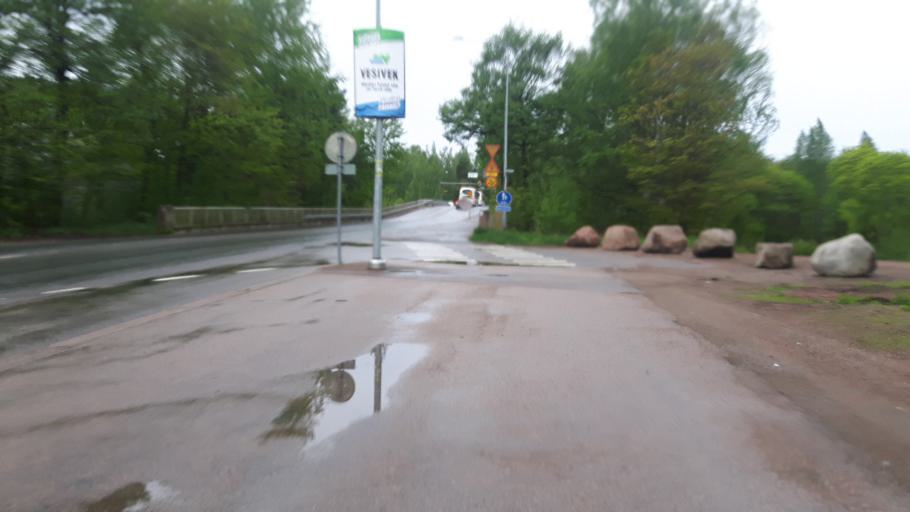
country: FI
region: Kymenlaakso
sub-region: Kotka-Hamina
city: Kotka
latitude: 60.4726
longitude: 26.9207
